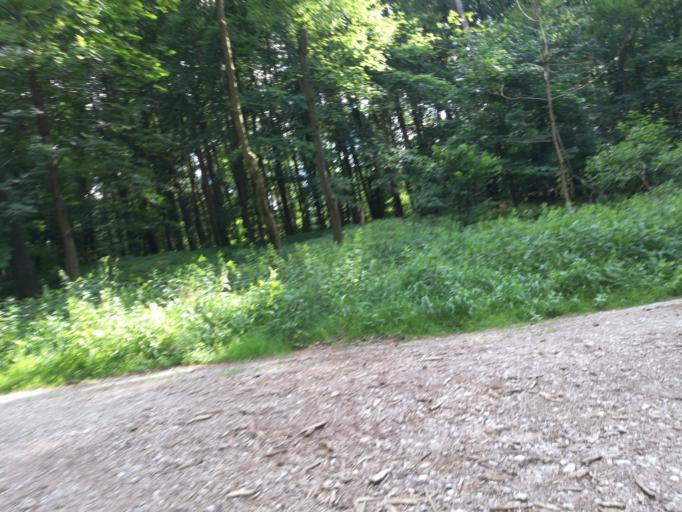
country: DE
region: Bavaria
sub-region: Regierungsbezirk Mittelfranken
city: Obermichelbach
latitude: 49.5046
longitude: 10.9192
